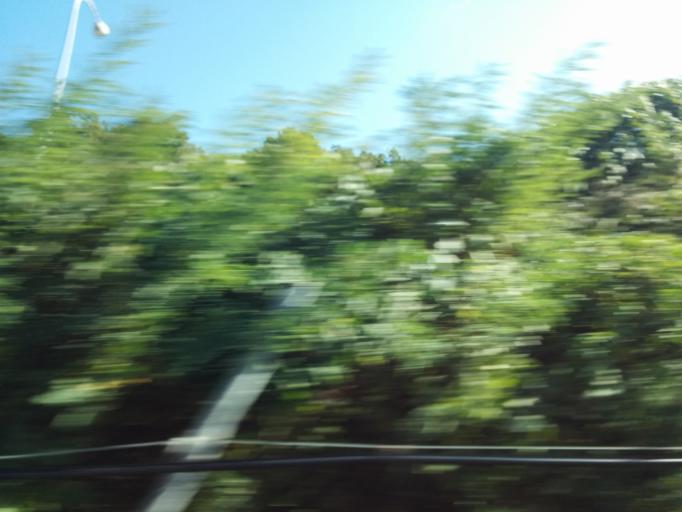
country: JP
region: Shiga Prefecture
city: Hikone
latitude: 35.2635
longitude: 136.2785
